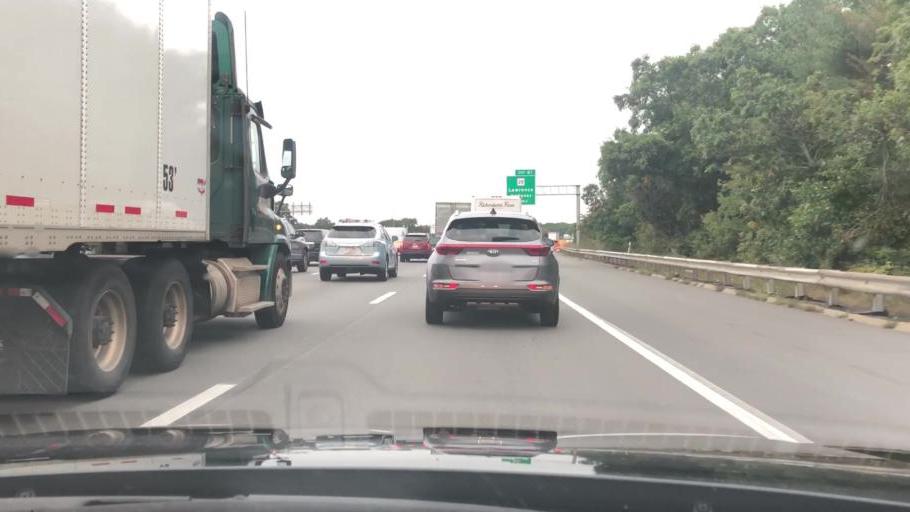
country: US
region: Massachusetts
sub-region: Essex County
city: North Andover
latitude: 42.6825
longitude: -71.1464
